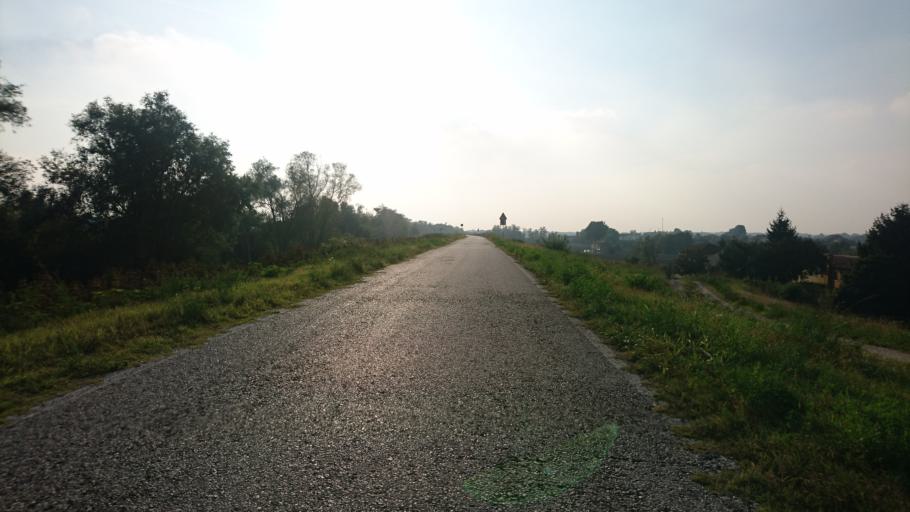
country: IT
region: Veneto
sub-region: Provincia di Rovigo
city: Canaro
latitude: 44.9279
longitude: 11.7124
